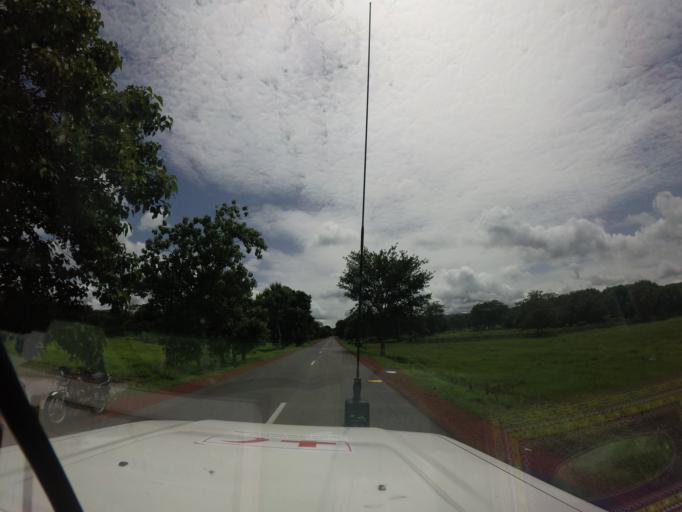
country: SL
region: Northern Province
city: Gberia Fotombu
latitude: 10.1634
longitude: -11.1917
